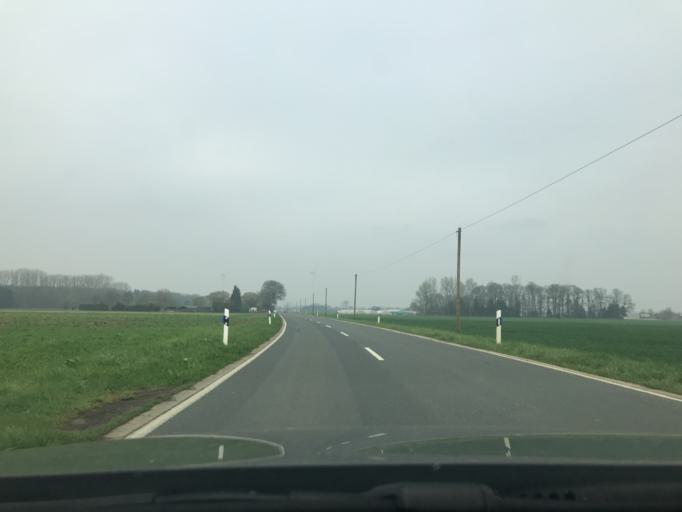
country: DE
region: North Rhine-Westphalia
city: Geldern
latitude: 51.4663
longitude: 6.3290
